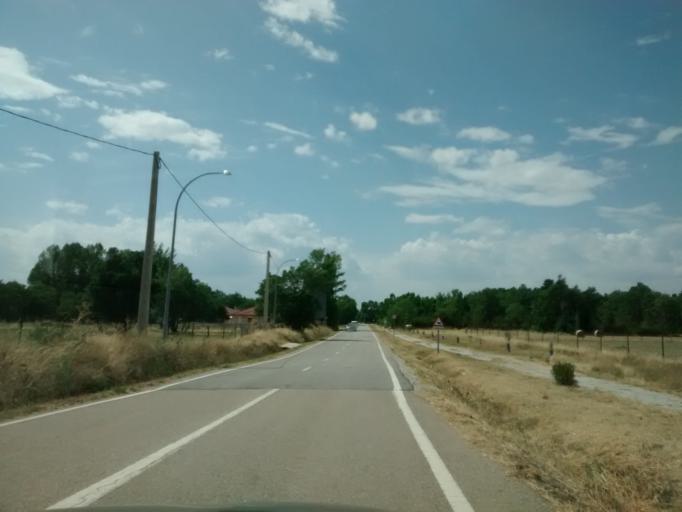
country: ES
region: Castille and Leon
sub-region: Provincia de Segovia
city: Matabuena
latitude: 41.0980
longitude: -3.7591
